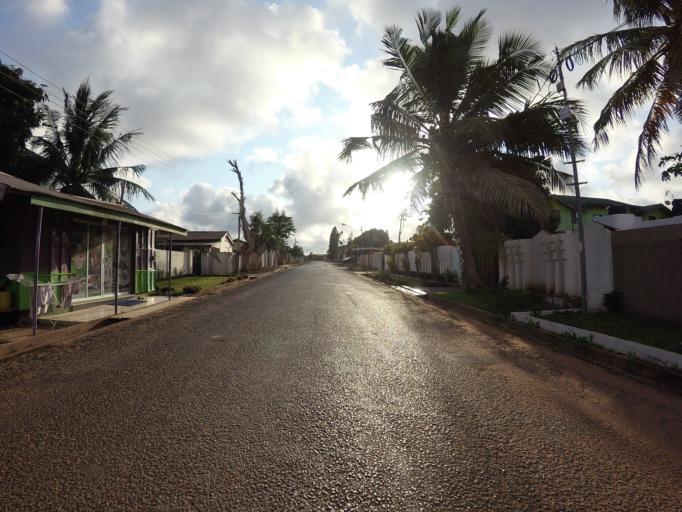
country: GH
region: Greater Accra
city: Nungua
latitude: 5.6128
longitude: -0.1020
